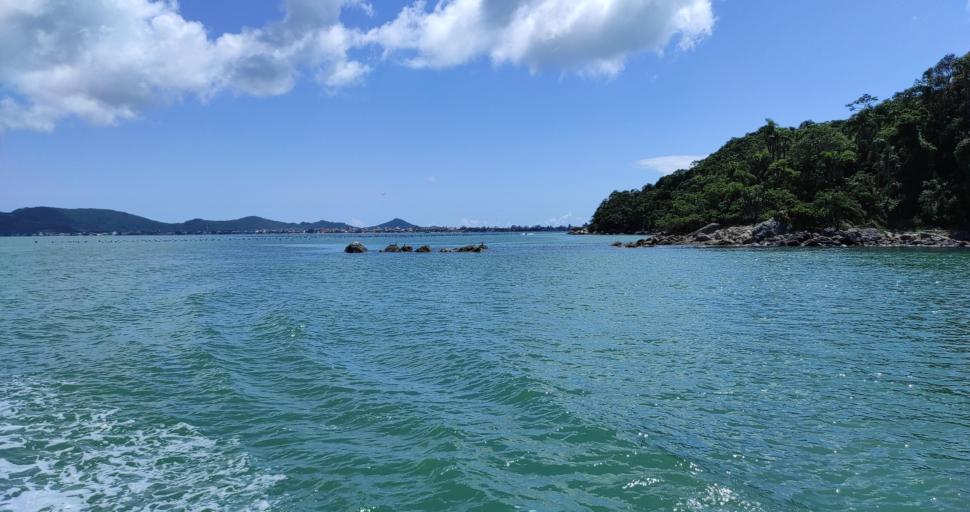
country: BR
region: Santa Catarina
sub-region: Porto Belo
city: Porto Belo
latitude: -27.2173
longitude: -48.5165
